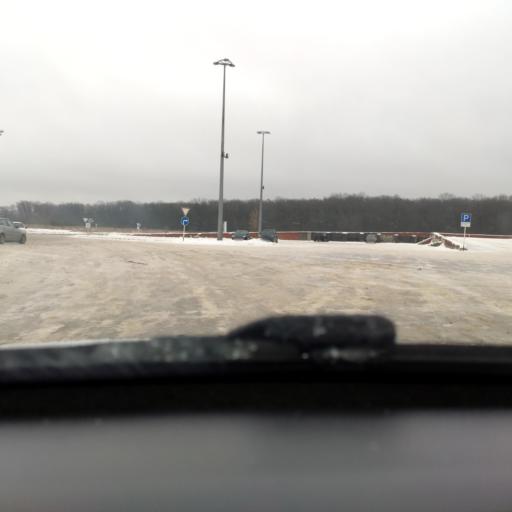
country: RU
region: Voronezj
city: Podgornoye
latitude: 51.7914
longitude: 39.2069
